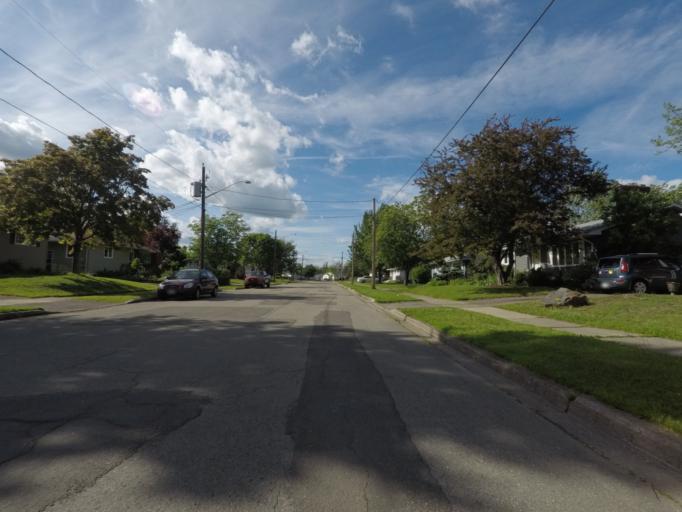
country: CA
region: New Brunswick
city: Moncton
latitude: 46.1023
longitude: -64.8262
